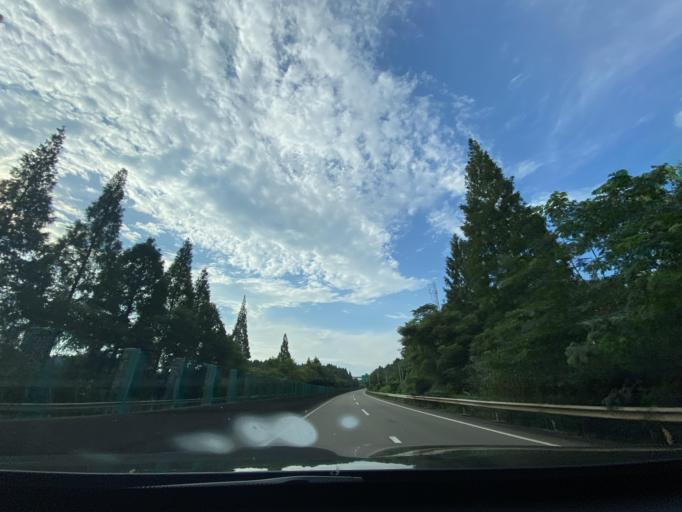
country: CN
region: Sichuan
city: Jiancheng
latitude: 30.2637
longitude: 104.6060
